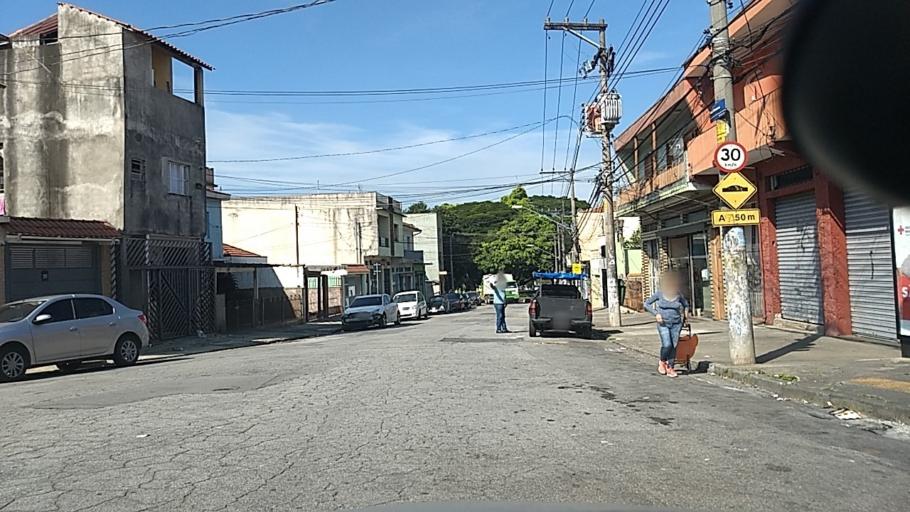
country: BR
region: Sao Paulo
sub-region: Guarulhos
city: Guarulhos
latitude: -23.5004
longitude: -46.5746
